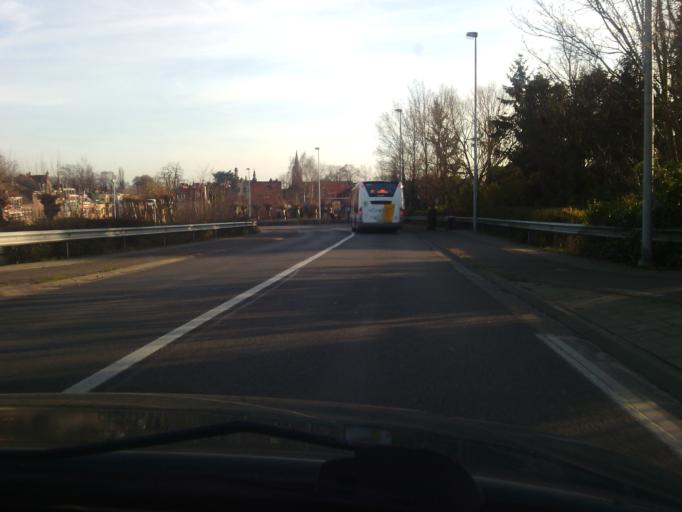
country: BE
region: Flanders
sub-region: Provincie Oost-Vlaanderen
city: Dendermonde
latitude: 51.0233
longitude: 4.1048
